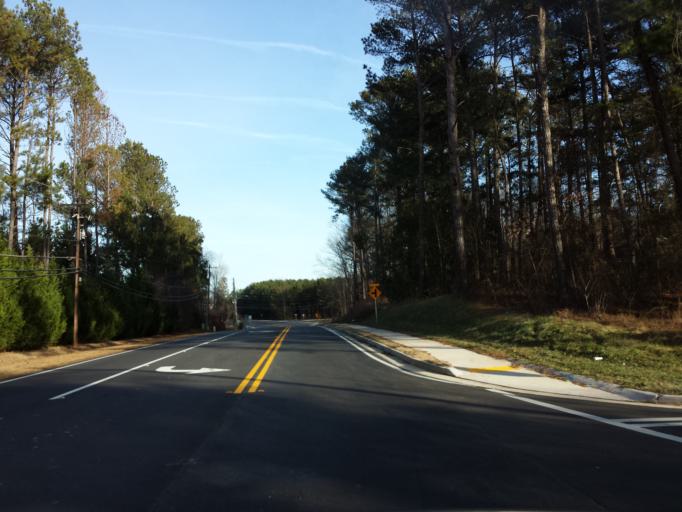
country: US
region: Georgia
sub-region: Cherokee County
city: Woodstock
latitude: 34.0682
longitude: -84.5301
